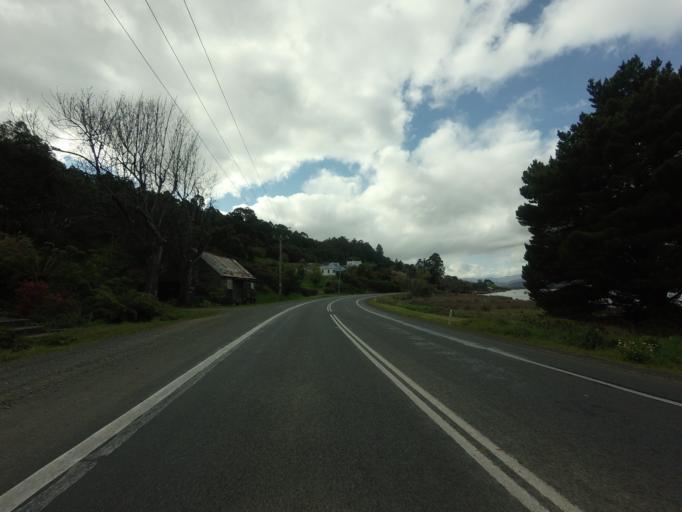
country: AU
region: Tasmania
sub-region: Huon Valley
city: Franklin
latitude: -43.1058
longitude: 147.0003
